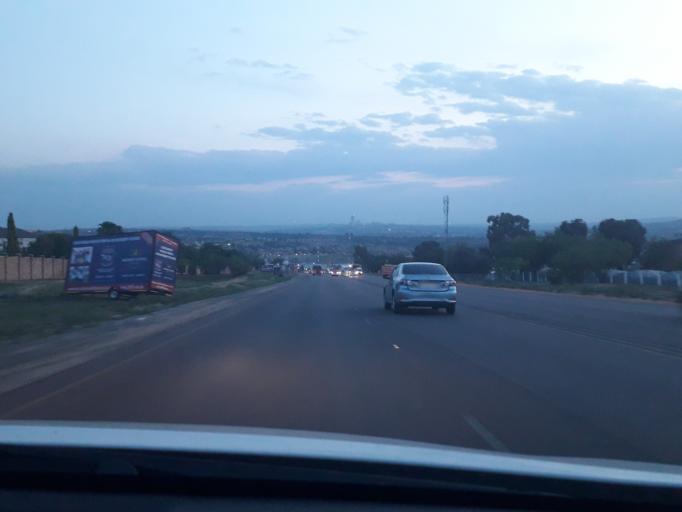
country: ZA
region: Gauteng
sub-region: City of Johannesburg Metropolitan Municipality
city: Midrand
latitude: -25.9929
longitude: 28.0766
